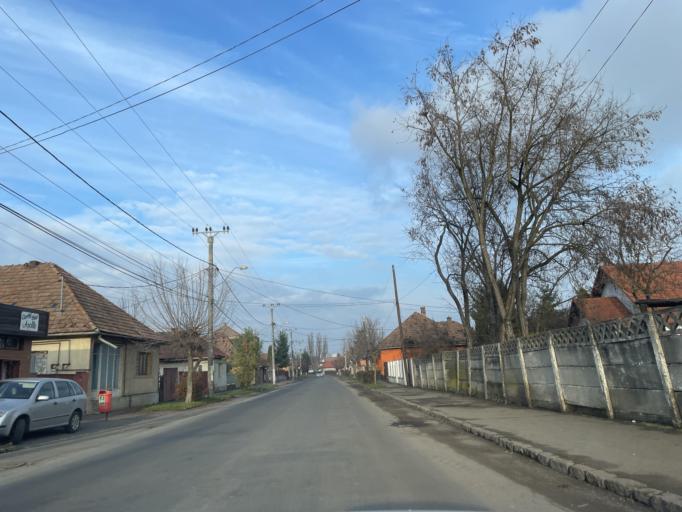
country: RO
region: Mures
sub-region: Municipiul Reghin
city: Reghin
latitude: 46.7675
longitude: 24.6962
